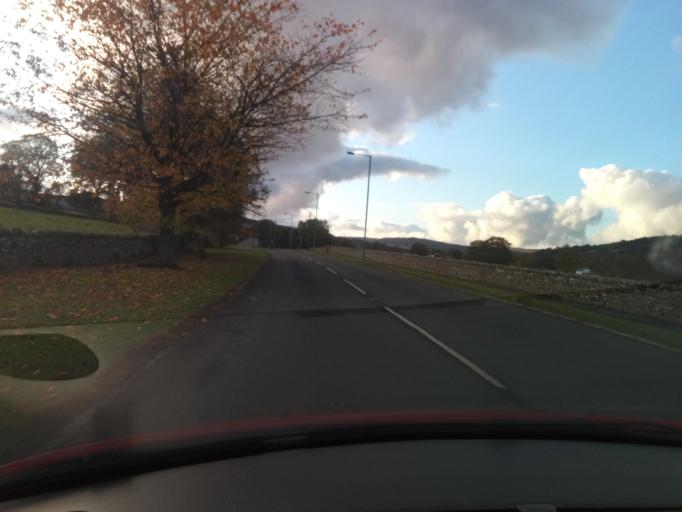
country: GB
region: England
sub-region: County Durham
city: Newbiggin
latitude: 54.7360
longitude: -2.1706
